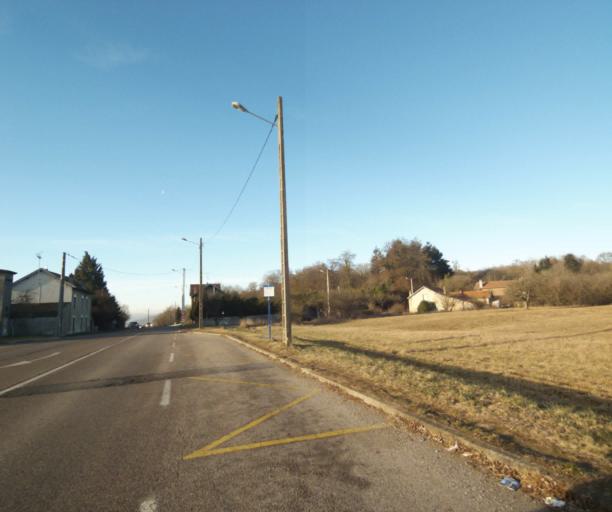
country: FR
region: Lorraine
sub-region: Departement de Meurthe-et-Moselle
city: Chavigny
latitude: 48.6379
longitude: 6.1302
